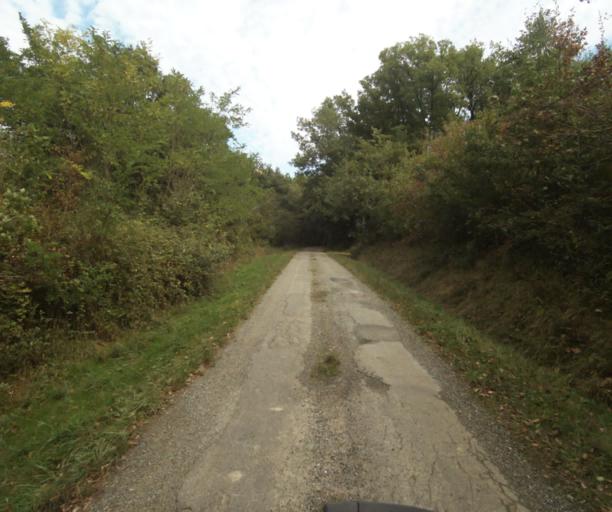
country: FR
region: Midi-Pyrenees
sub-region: Departement du Tarn-et-Garonne
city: Verdun-sur-Garonne
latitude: 43.8659
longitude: 1.1908
